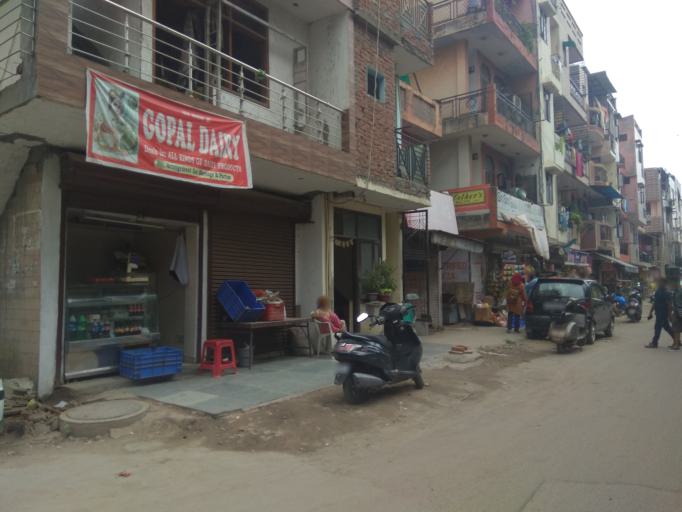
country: IN
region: NCT
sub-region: New Delhi
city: New Delhi
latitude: 28.5723
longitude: 77.2536
